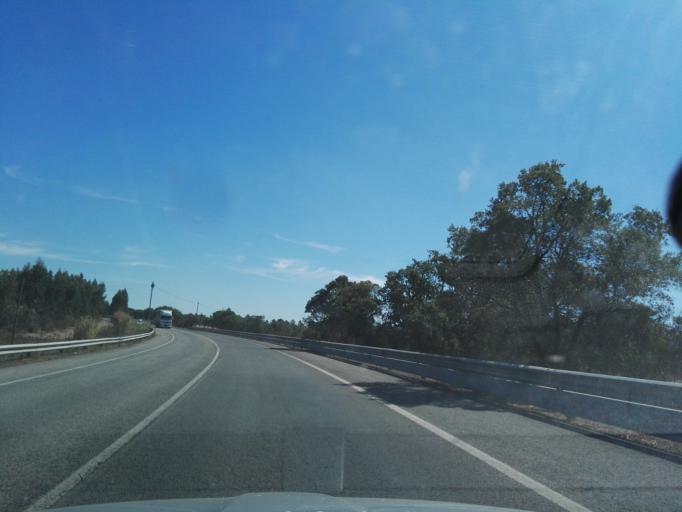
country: PT
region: Santarem
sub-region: Benavente
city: Poceirao
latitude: 38.8469
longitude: -8.7685
